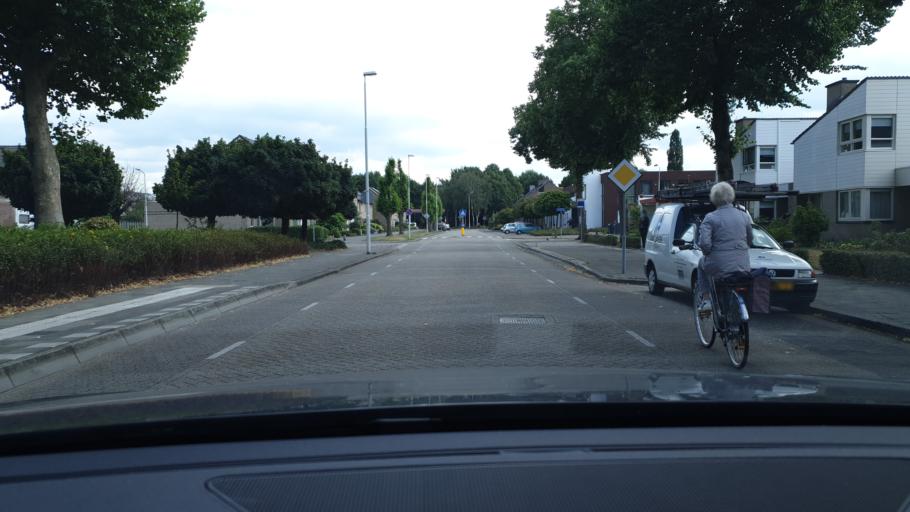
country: NL
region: North Brabant
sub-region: Gemeente Best
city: Best
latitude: 51.5098
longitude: 5.3993
